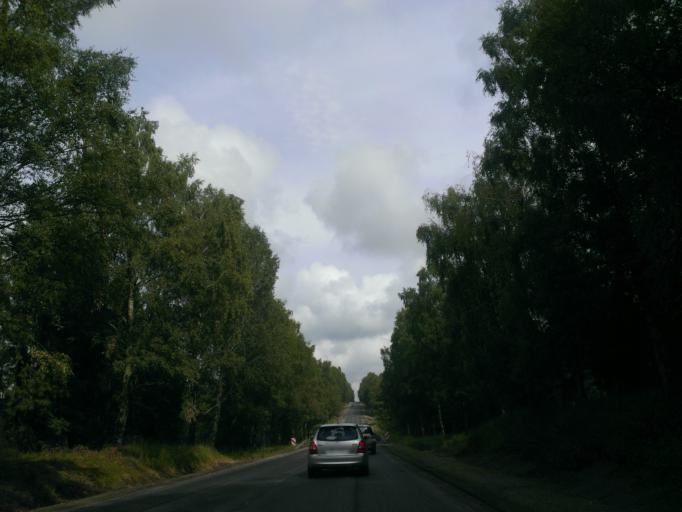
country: LV
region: Ligatne
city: Ligatne
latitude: 57.1942
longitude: 25.0889
